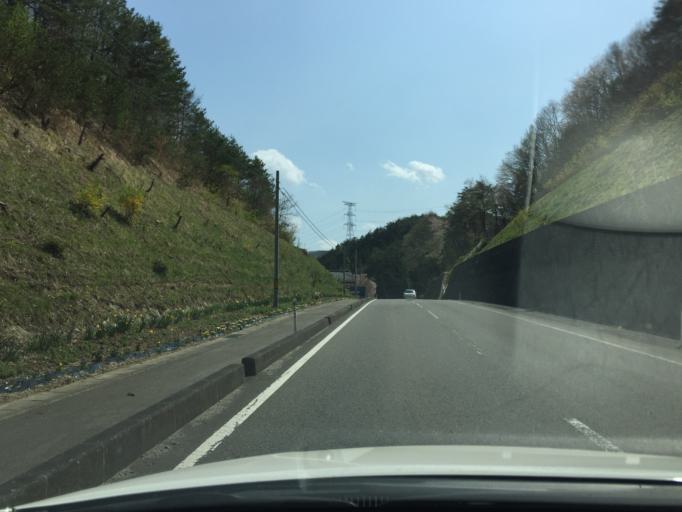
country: JP
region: Fukushima
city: Funehikimachi-funehiki
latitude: 37.4220
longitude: 140.7908
